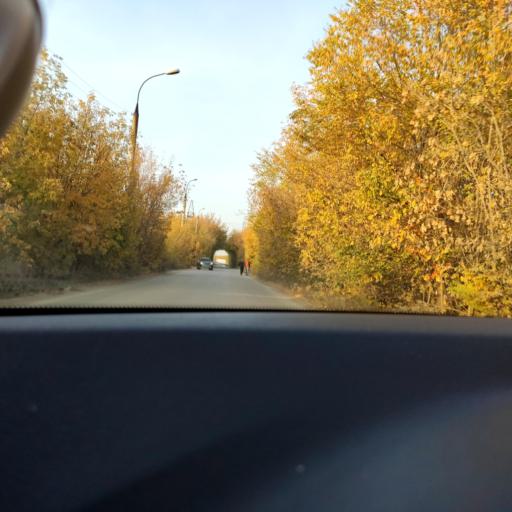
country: RU
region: Samara
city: Petra-Dubrava
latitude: 53.2594
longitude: 50.2974
